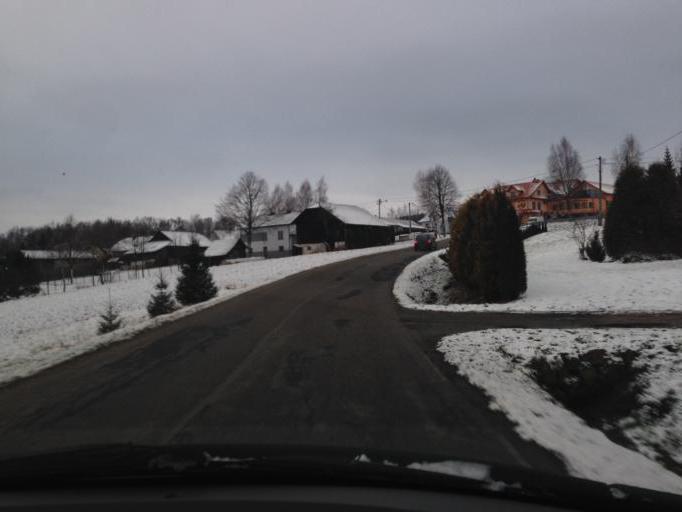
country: PL
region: Lesser Poland Voivodeship
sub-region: Powiat gorlicki
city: Moszczenica
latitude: 49.7433
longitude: 21.0838
